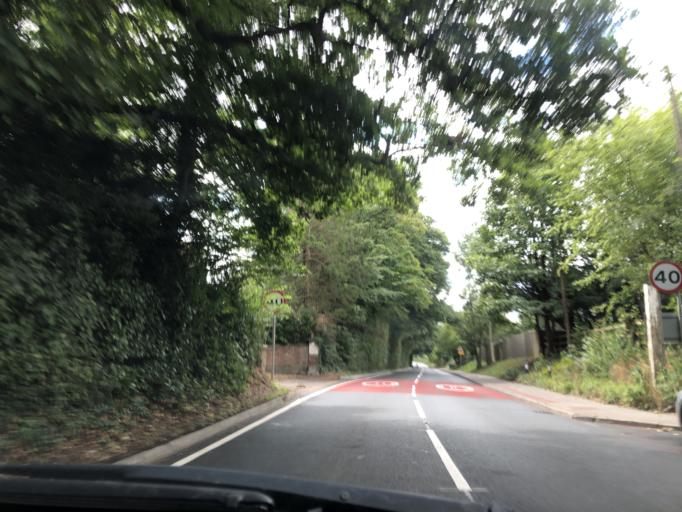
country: GB
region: England
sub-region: Kent
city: Westerham
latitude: 51.2342
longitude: 0.0639
